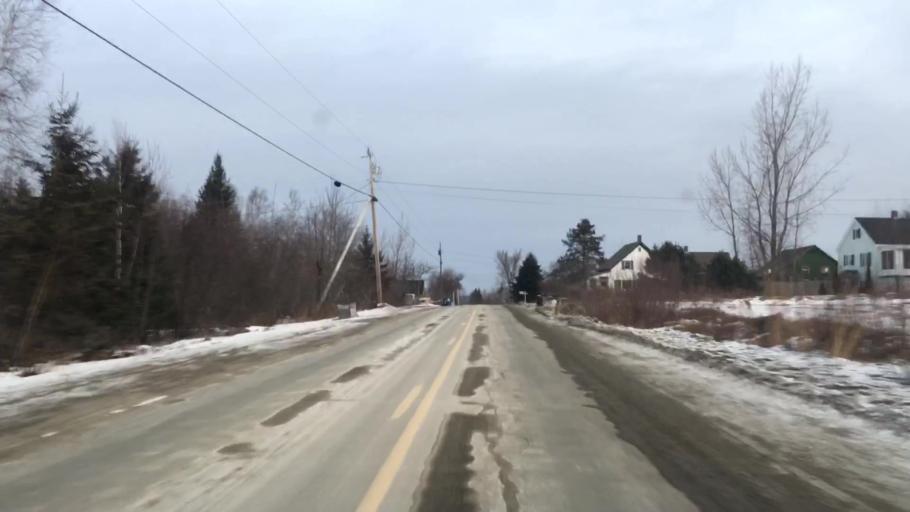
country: US
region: Maine
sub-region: Hancock County
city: Franklin
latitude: 44.7314
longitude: -68.3357
